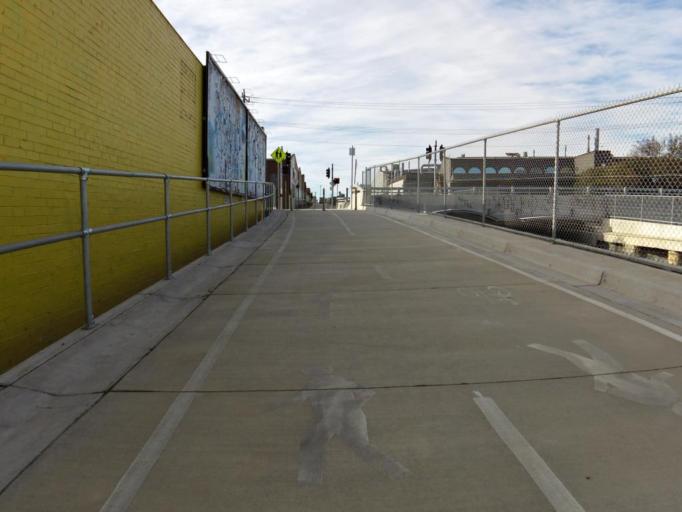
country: AU
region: Victoria
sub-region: Whitehorse
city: Nunawading
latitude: -37.8190
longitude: 145.1850
